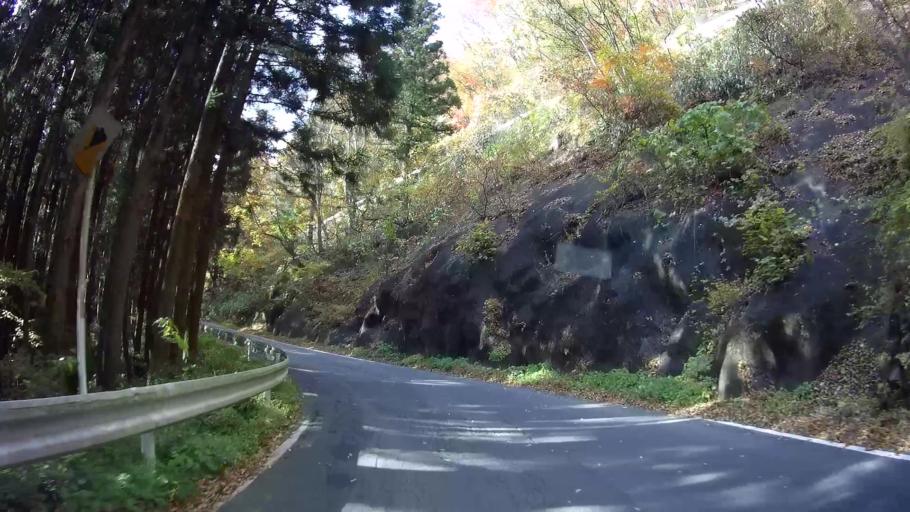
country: JP
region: Gunma
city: Nakanojomachi
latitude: 36.6164
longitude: 138.6369
